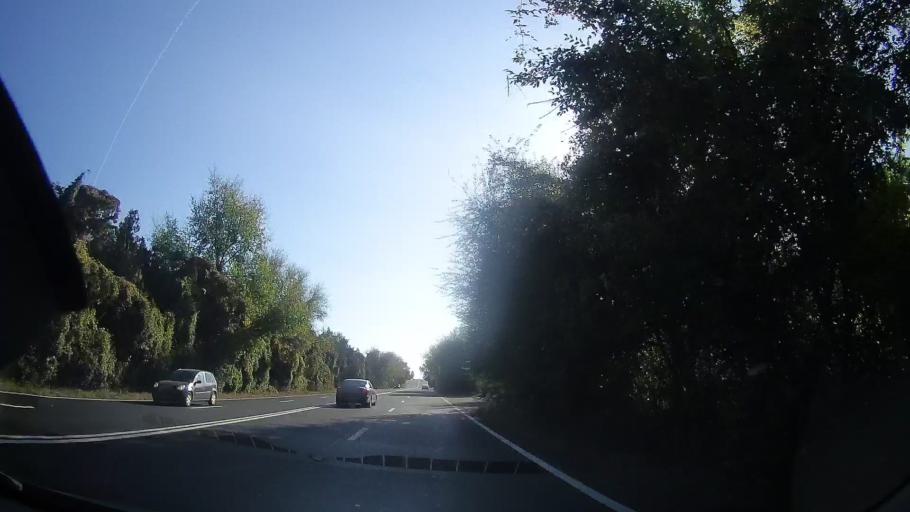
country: RO
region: Constanta
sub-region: Comuna Douazeci si Trei August
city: Dulcesti
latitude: 43.8640
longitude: 28.5752
